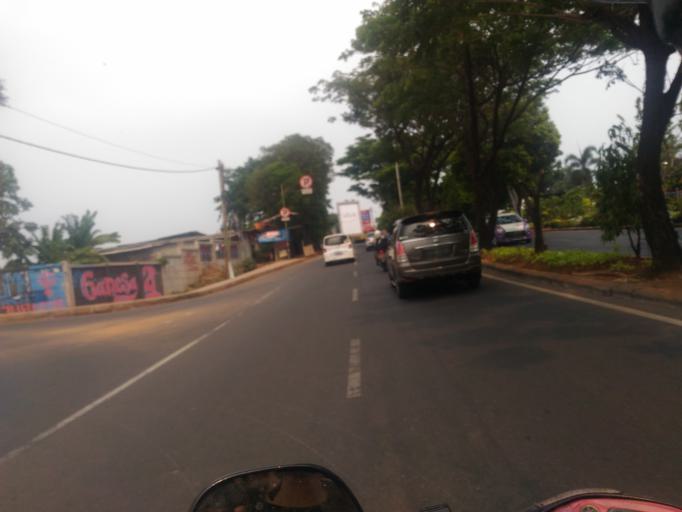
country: ID
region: West Java
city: Depok
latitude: -6.3795
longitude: 106.8502
